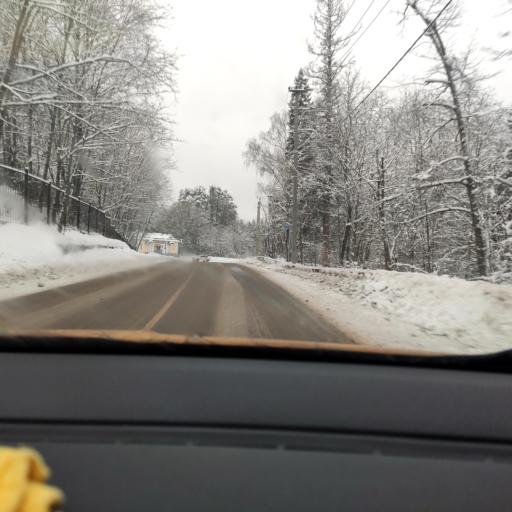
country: RU
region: Moskovskaya
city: Yershovo
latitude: 55.7729
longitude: 36.7970
